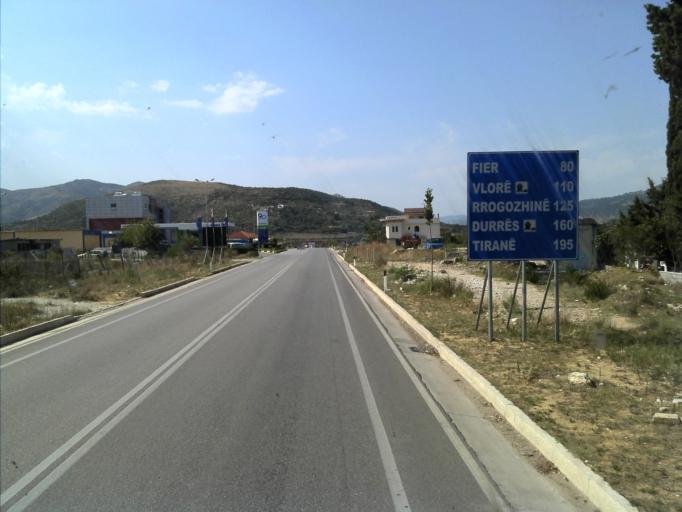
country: AL
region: Gjirokaster
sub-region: Rrethi i Tepelenes
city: Tepelene
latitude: 40.3023
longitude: 20.0209
